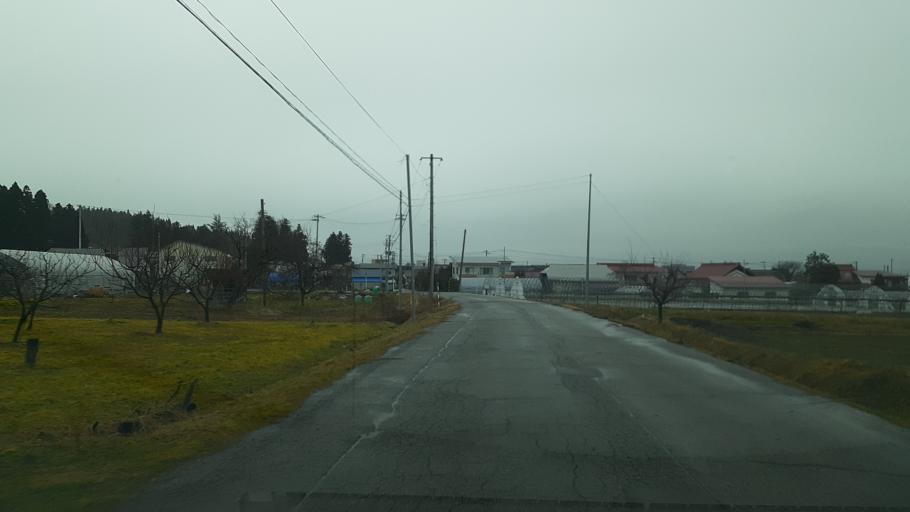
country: JP
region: Fukushima
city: Kitakata
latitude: 37.4997
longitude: 139.8234
